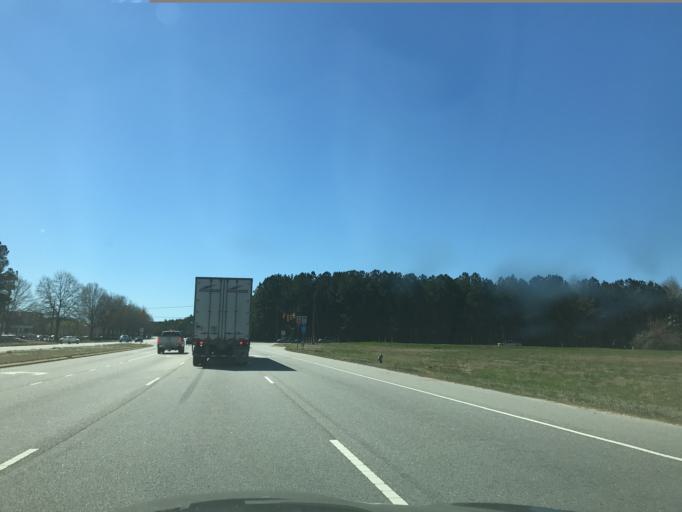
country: US
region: North Carolina
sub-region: Wake County
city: Garner
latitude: 35.7321
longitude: -78.6408
